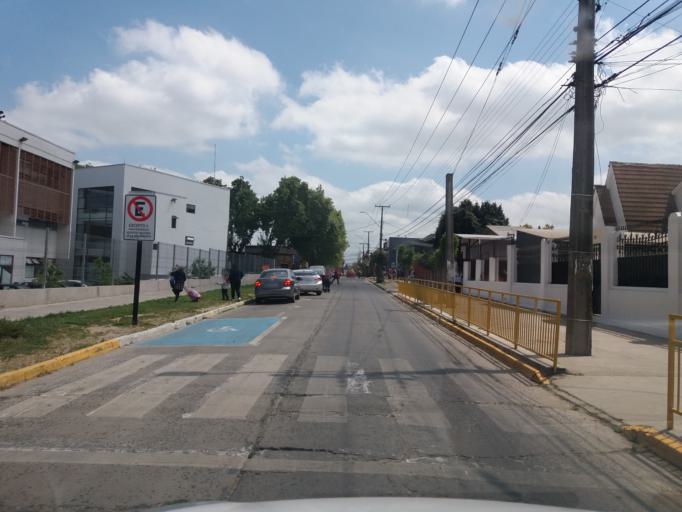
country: CL
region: Valparaiso
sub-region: Provincia de Marga Marga
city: Limache
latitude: -32.9849
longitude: -71.2729
